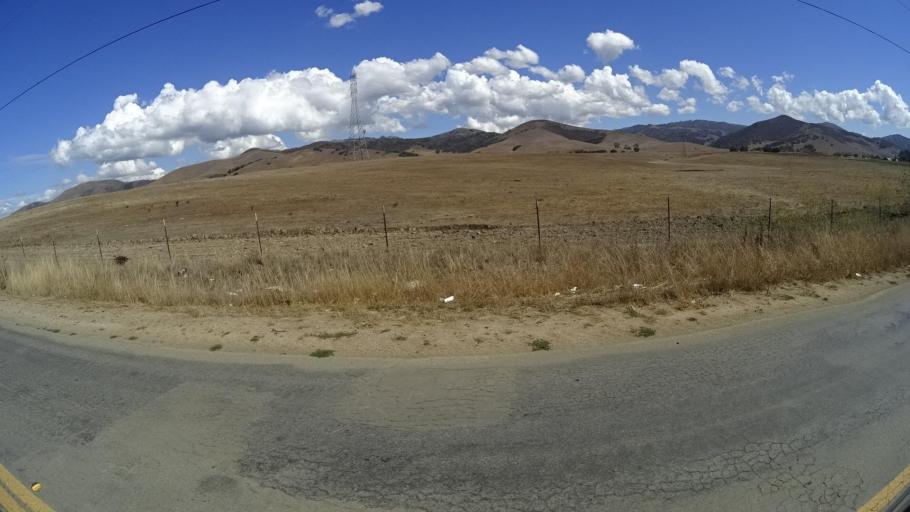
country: US
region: California
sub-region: Monterey County
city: Salinas
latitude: 36.6990
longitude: -121.5765
